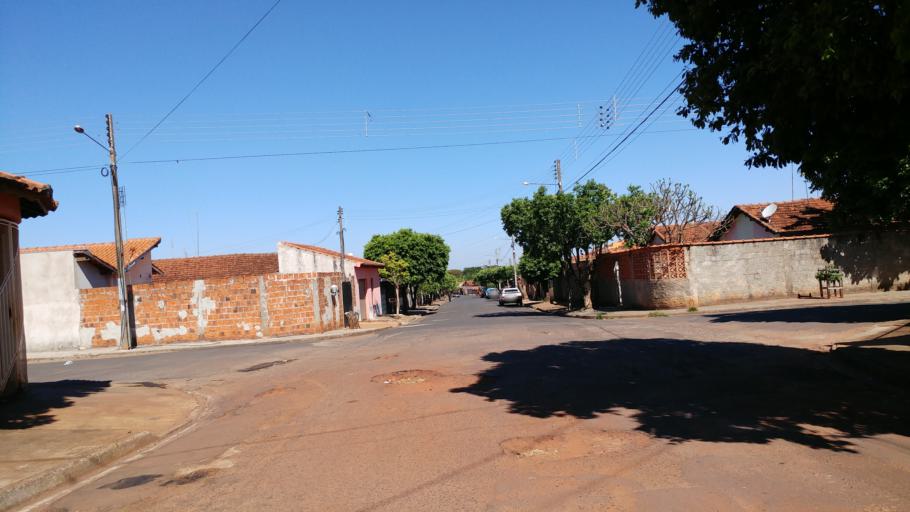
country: BR
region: Sao Paulo
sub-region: Paraguacu Paulista
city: Paraguacu Paulista
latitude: -22.4373
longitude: -50.5835
